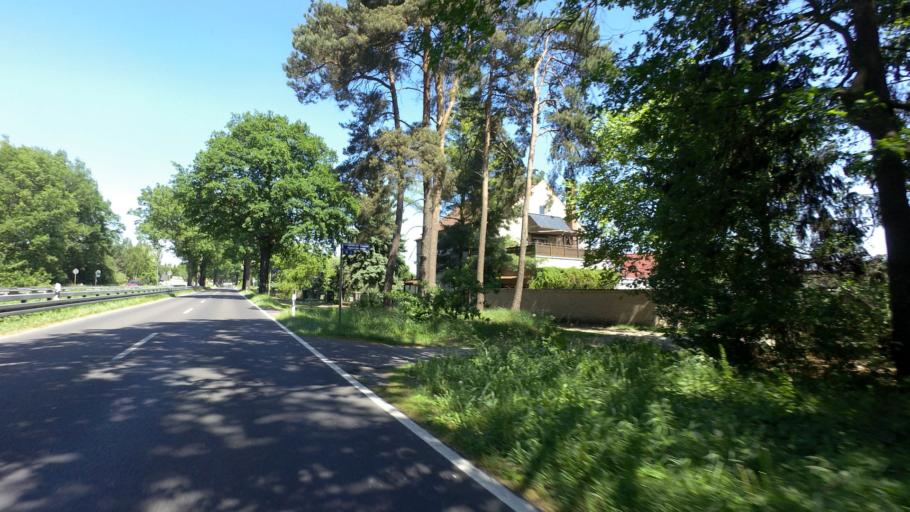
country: DE
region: Brandenburg
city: Peitz
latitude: 51.8009
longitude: 14.3824
